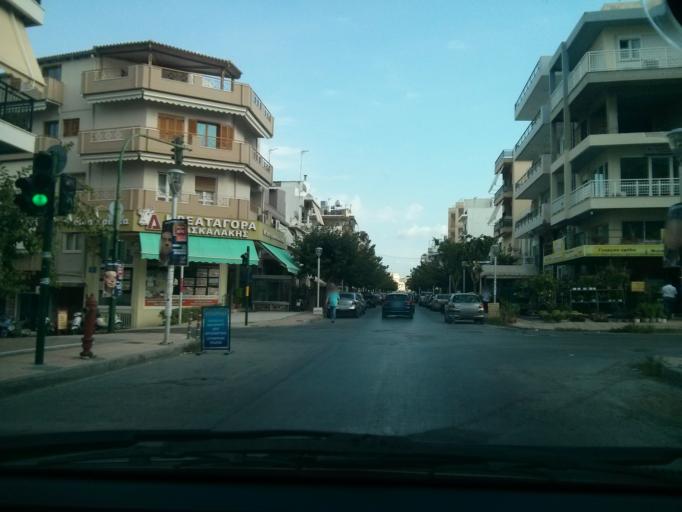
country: GR
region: Crete
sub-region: Nomos Irakleiou
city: Irakleion
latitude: 35.3311
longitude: 25.1357
